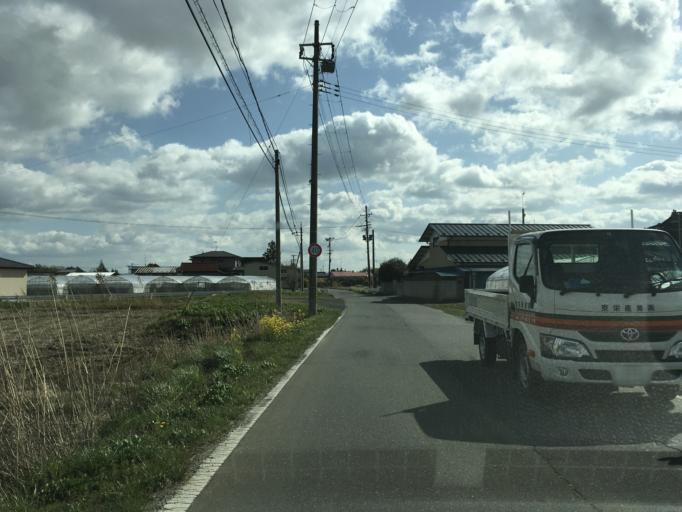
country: JP
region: Iwate
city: Ichinoseki
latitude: 38.7398
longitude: 141.2660
